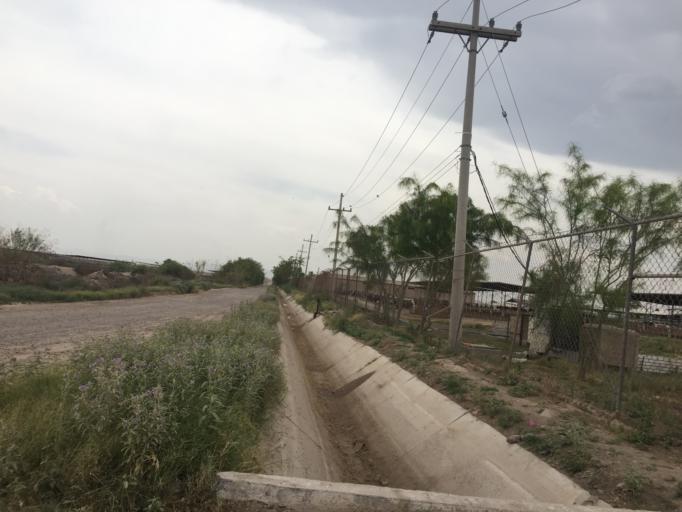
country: MX
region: Durango
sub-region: Gomez Palacio
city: San Jose de Vinedo
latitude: 25.6715
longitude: -103.4398
